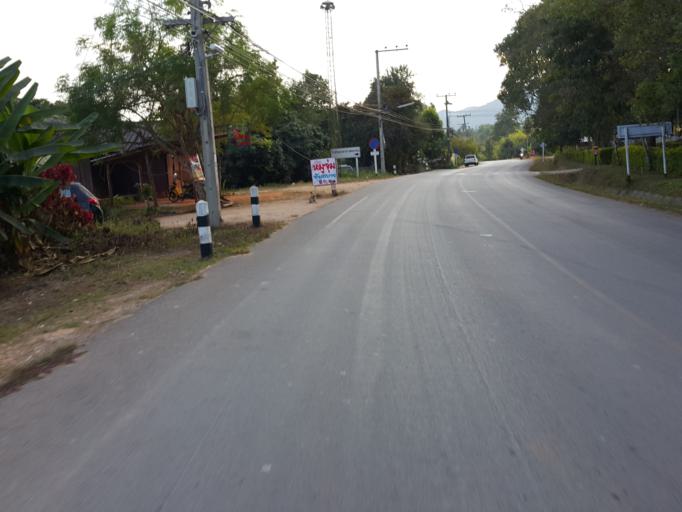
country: TH
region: Lamphun
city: Thung Hua Chang
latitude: 18.0165
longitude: 99.0267
